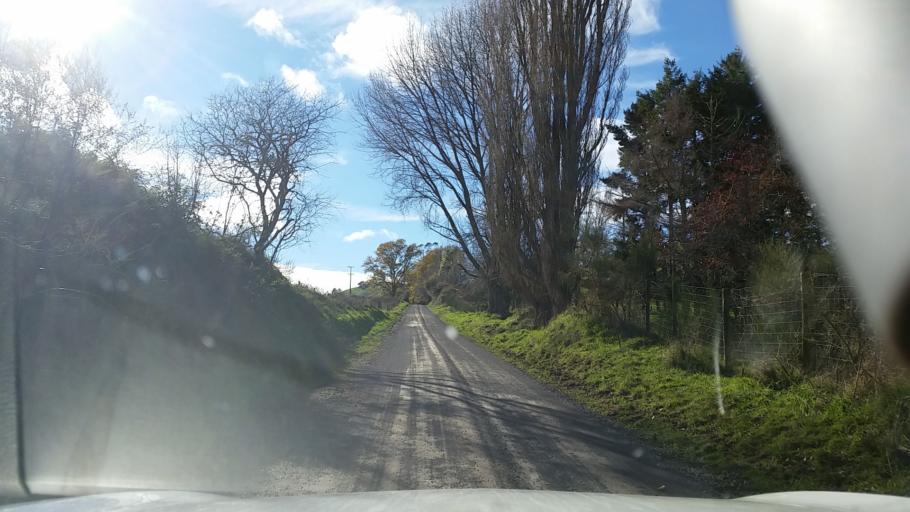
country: NZ
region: Bay of Plenty
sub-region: Rotorua District
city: Rotorua
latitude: -38.3873
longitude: 176.1958
